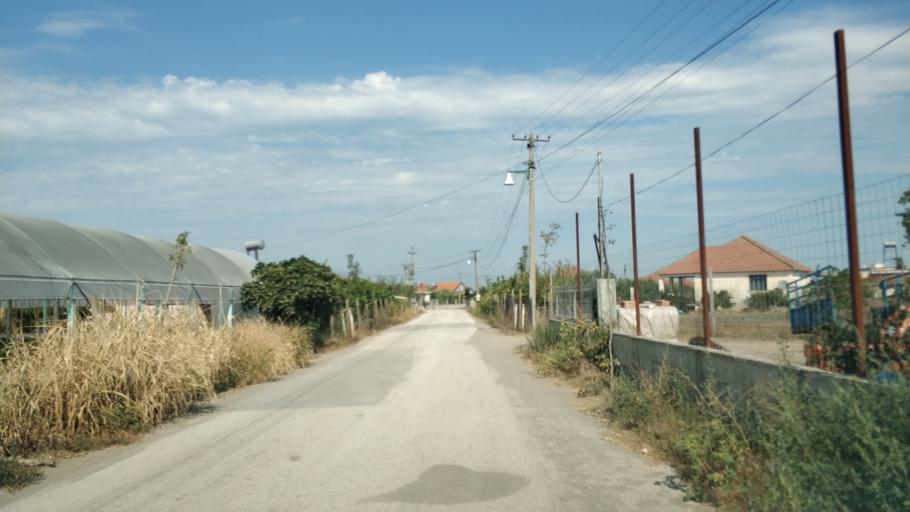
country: AL
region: Fier
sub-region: Rrethi i Lushnjes
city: Divjake
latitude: 40.9897
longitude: 19.5267
